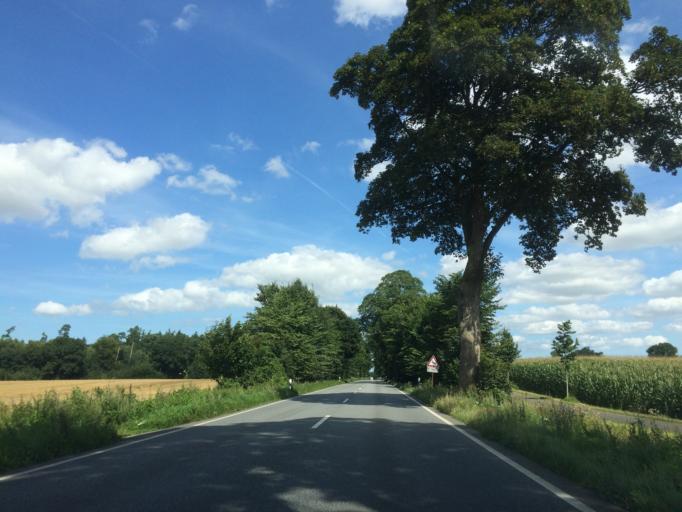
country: DE
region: Schleswig-Holstein
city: Grebin
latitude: 54.1966
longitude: 10.4673
